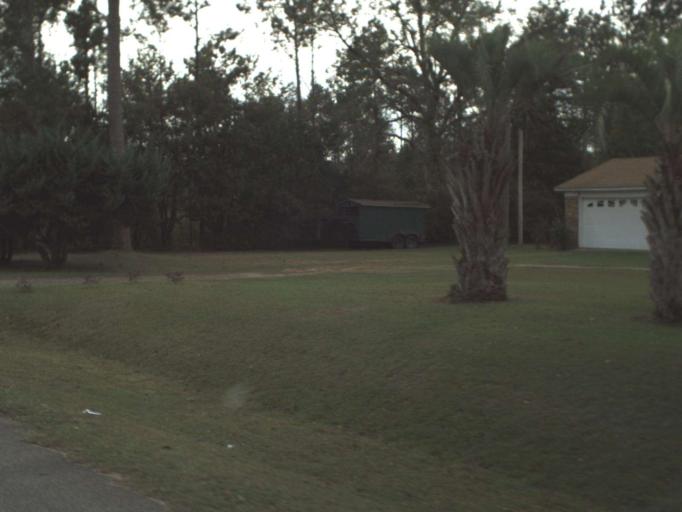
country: US
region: Florida
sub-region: Gadsden County
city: Quincy
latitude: 30.6467
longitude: -84.6007
